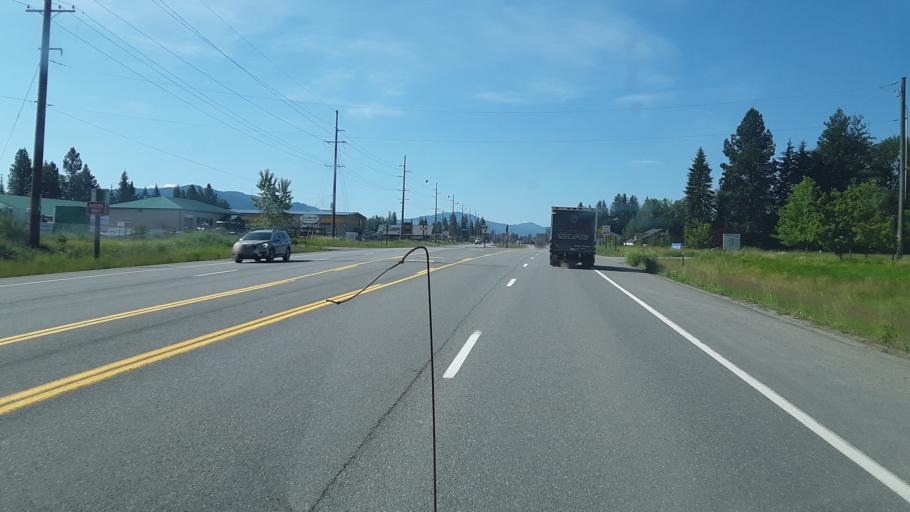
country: US
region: Idaho
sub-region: Bonner County
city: Ponderay
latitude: 48.3149
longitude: -116.5463
